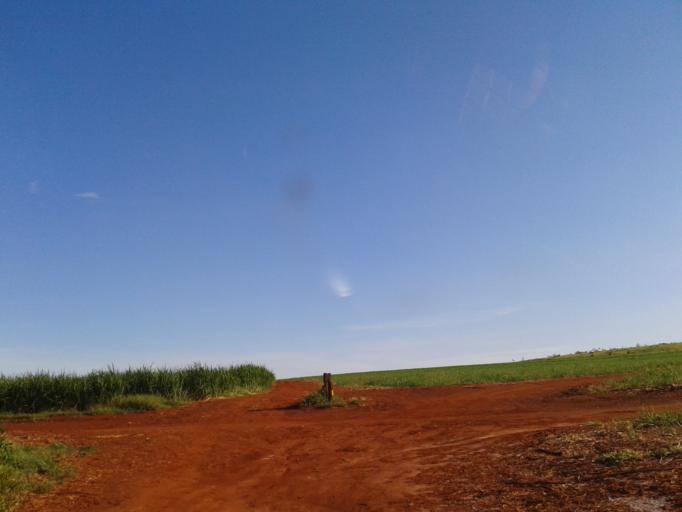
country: BR
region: Minas Gerais
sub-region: Centralina
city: Centralina
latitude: -18.6729
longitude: -49.2718
